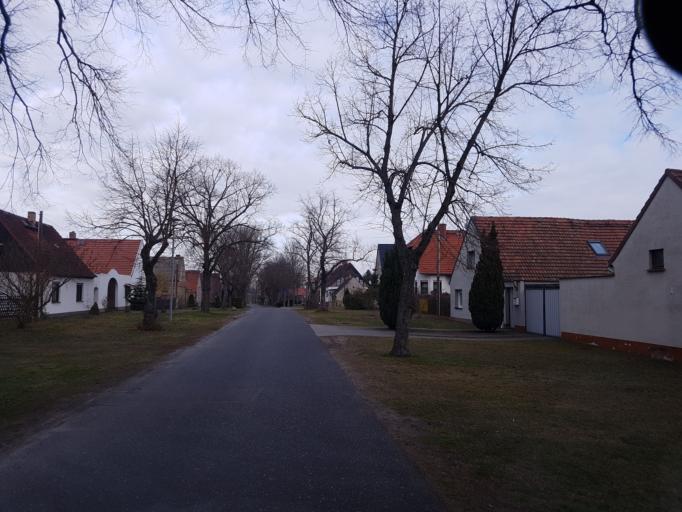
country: DE
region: Brandenburg
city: Finsterwalde
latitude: 51.6160
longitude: 13.7627
